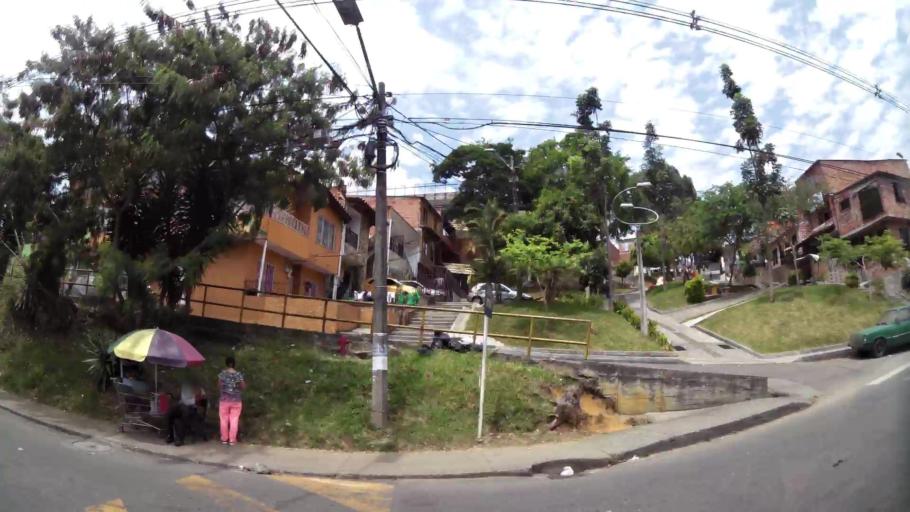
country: CO
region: Antioquia
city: Bello
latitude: 6.3060
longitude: -75.5768
